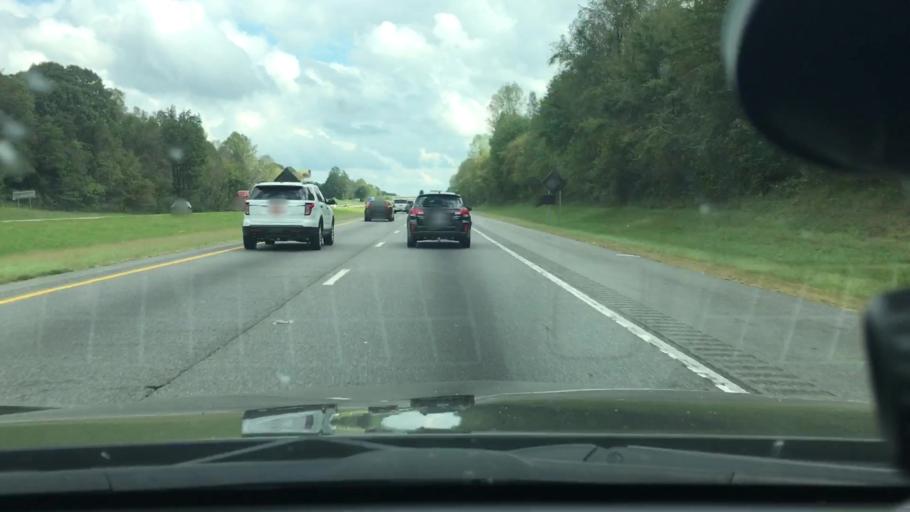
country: US
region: North Carolina
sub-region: Catawba County
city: Conover
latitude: 35.7093
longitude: -81.2401
